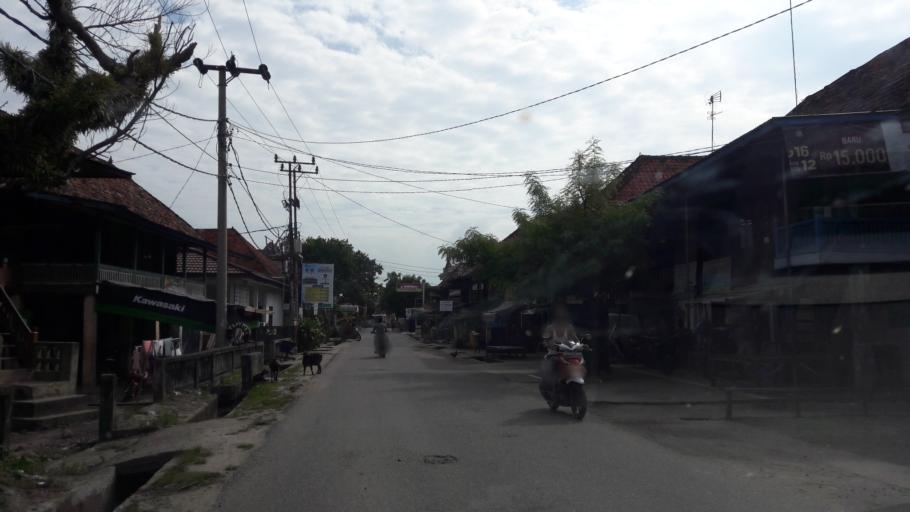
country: ID
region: South Sumatra
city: Gunungmenang
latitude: -3.0904
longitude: 104.0198
